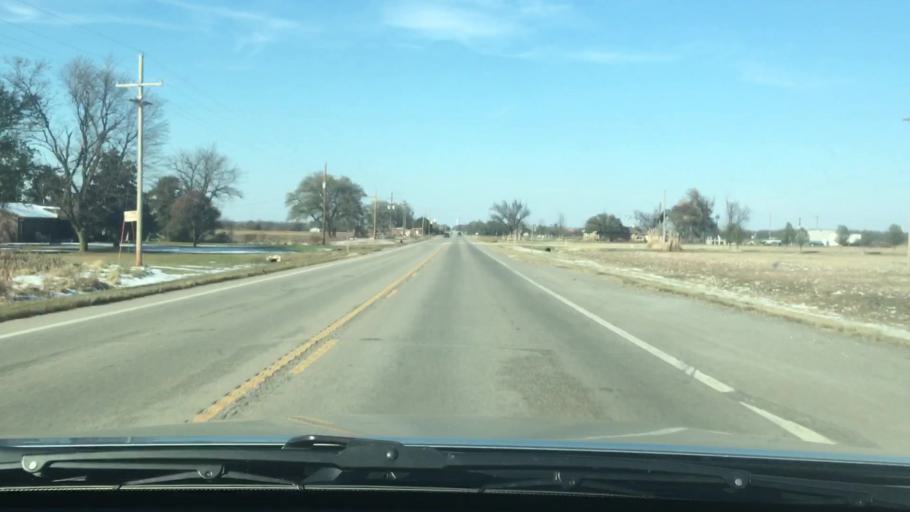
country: US
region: Kansas
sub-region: Rice County
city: Lyons
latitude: 38.3159
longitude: -98.2018
